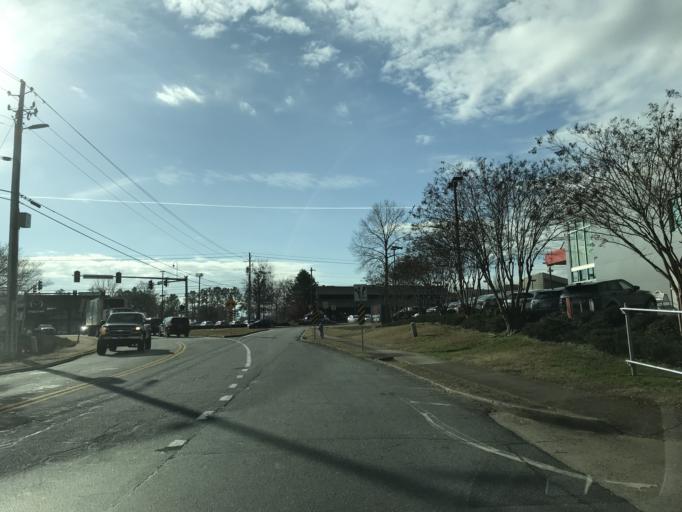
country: US
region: Georgia
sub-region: Fulton County
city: Roswell
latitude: 34.0526
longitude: -84.3347
